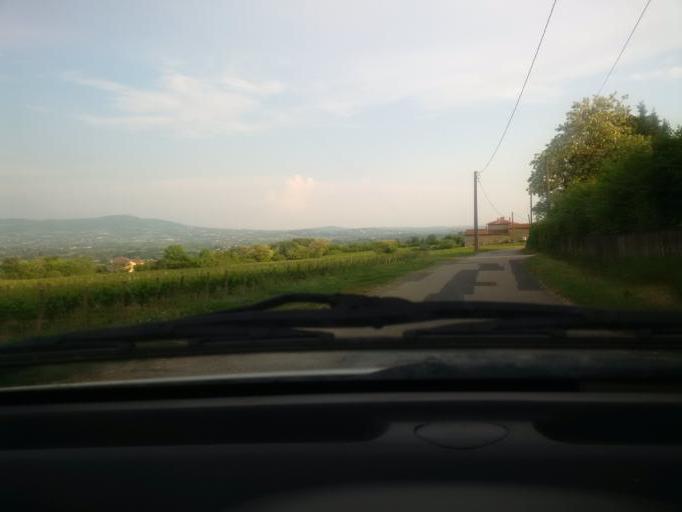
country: FR
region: Rhone-Alpes
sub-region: Departement du Rhone
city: Lucenay
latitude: 45.9228
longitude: 4.6988
